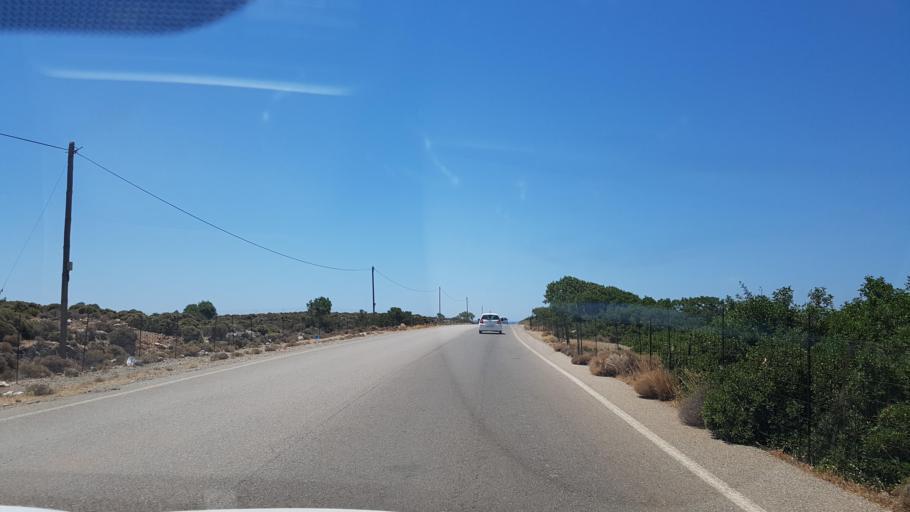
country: GR
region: Crete
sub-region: Nomos Chanias
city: Palaiochora
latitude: 35.2825
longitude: 23.5474
